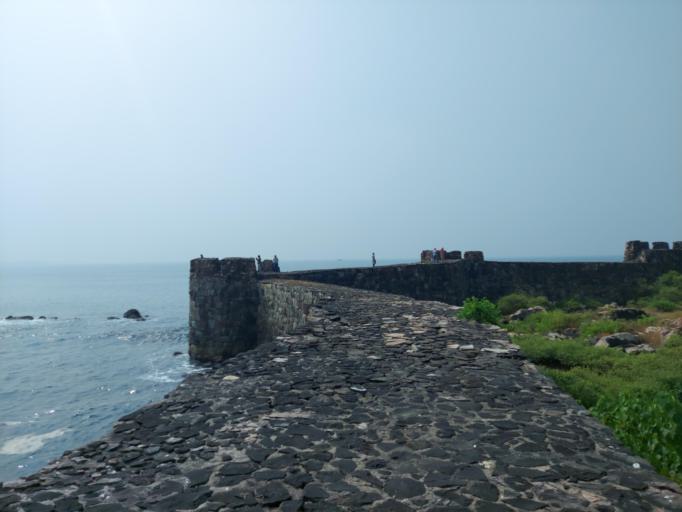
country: IN
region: Maharashtra
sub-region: Sindhudurg
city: Malvan
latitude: 16.0398
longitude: 73.4610
